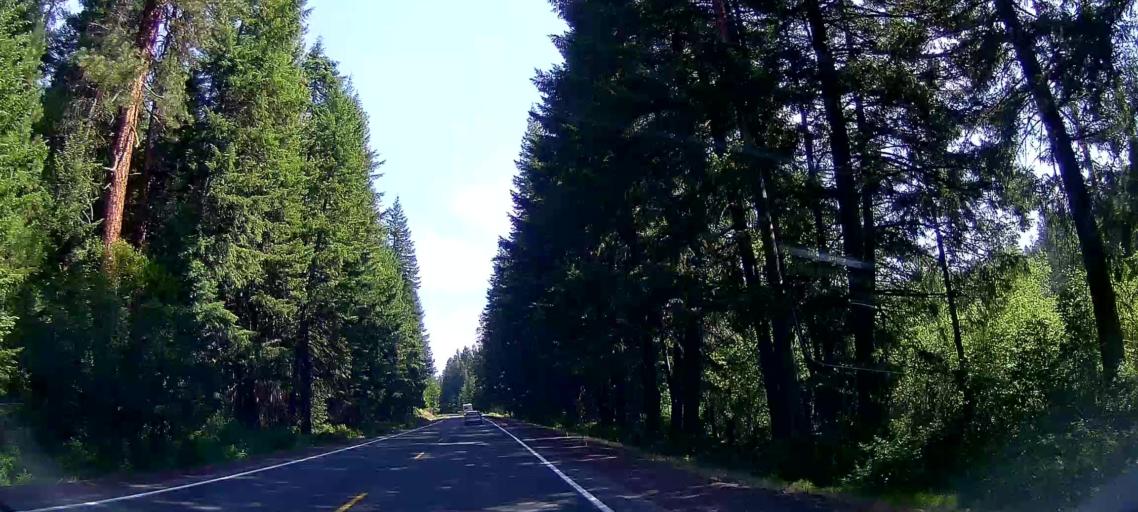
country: US
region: Oregon
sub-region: Jefferson County
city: Warm Springs
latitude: 45.0295
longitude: -121.5125
